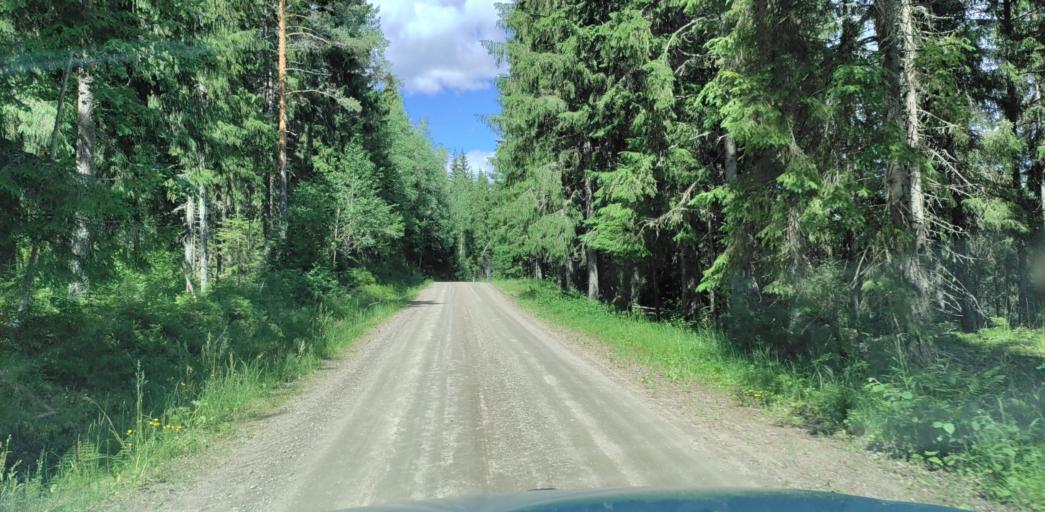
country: SE
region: Vaermland
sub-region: Sunne Kommun
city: Sunne
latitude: 60.0465
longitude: 13.2567
